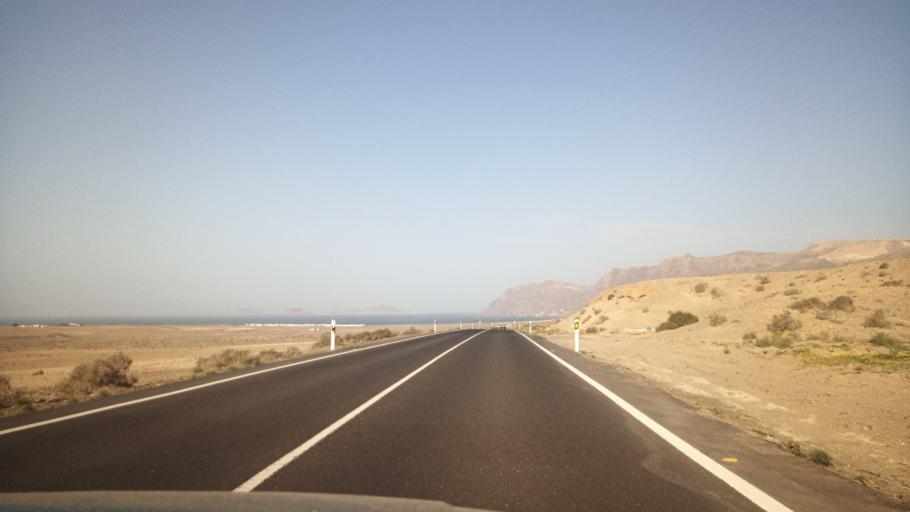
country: ES
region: Canary Islands
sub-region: Provincia de Las Palmas
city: Teguise
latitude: 29.0773
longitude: -13.5771
